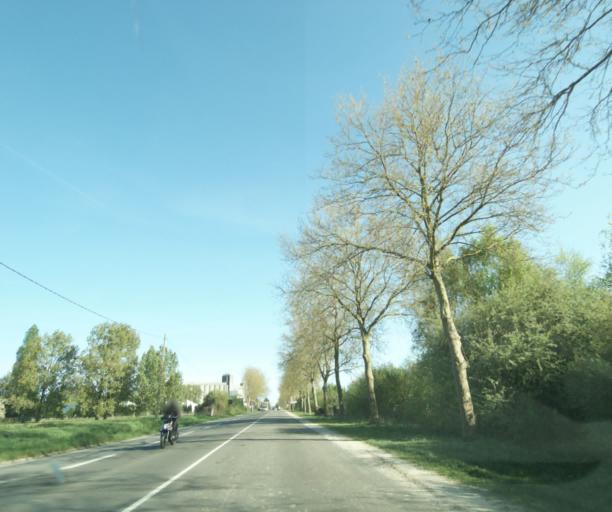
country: FR
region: Ile-de-France
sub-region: Departement de Seine-et-Marne
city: Nangis
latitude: 48.5667
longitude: 3.0064
